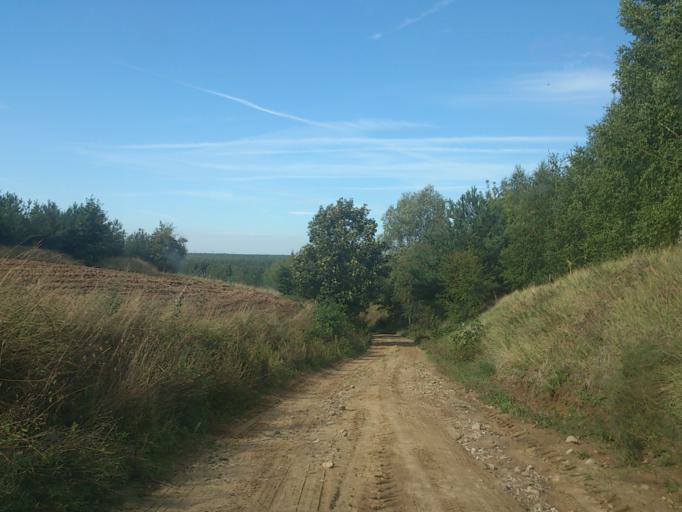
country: PL
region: Kujawsko-Pomorskie
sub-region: Powiat golubsko-dobrzynski
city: Radomin
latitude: 53.1218
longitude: 19.1315
